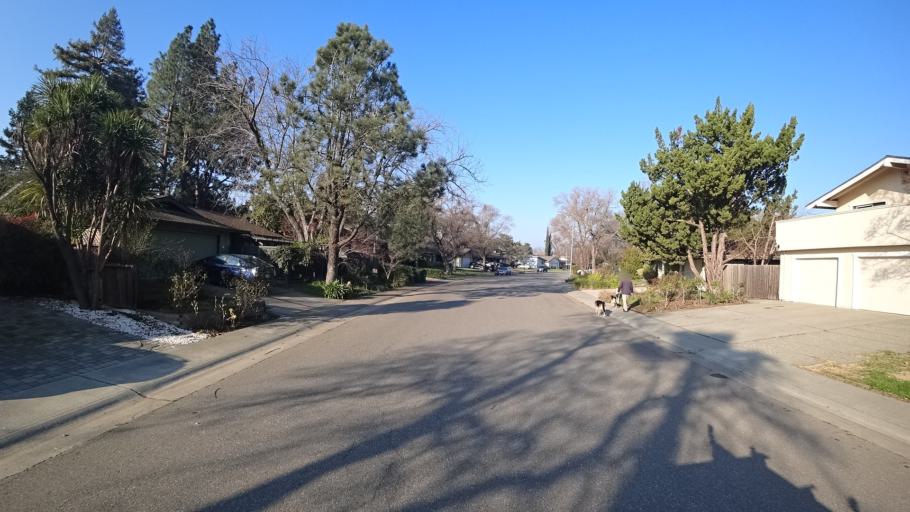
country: US
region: California
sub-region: Yolo County
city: Davis
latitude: 38.5481
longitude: -121.7907
